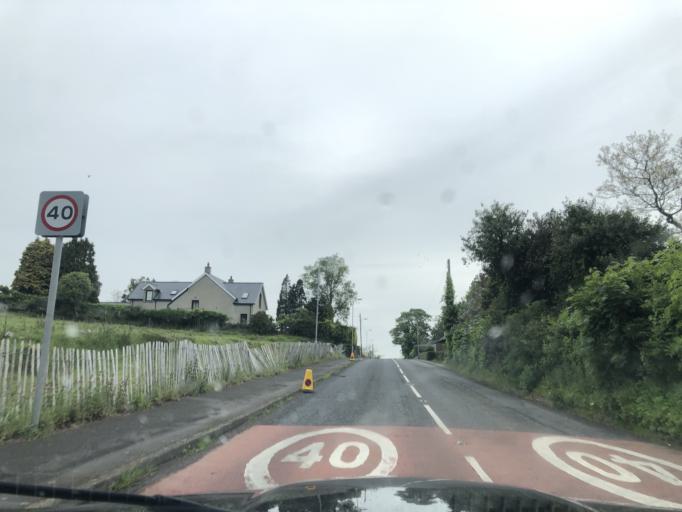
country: GB
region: Northern Ireland
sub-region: Down District
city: Castlewellan
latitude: 54.2289
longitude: -5.9349
